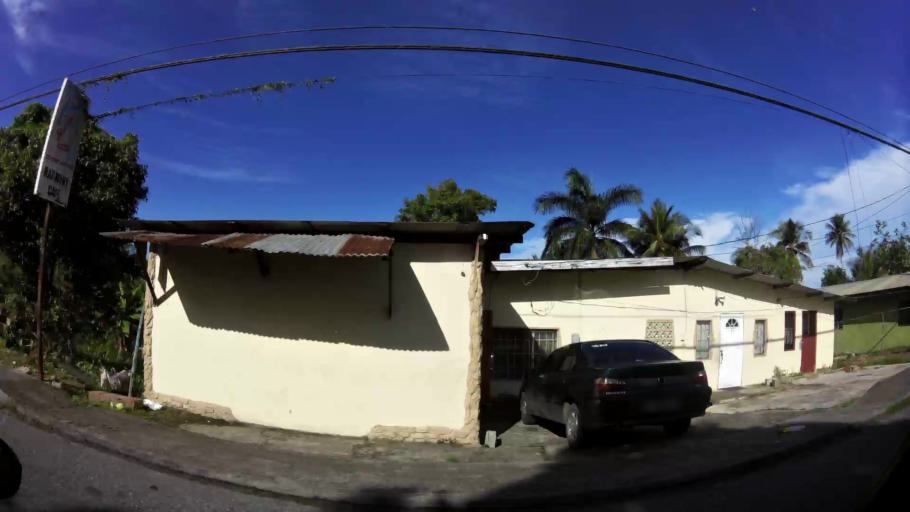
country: TT
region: Chaguanas
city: Chaguanas
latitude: 10.5157
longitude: -61.3869
